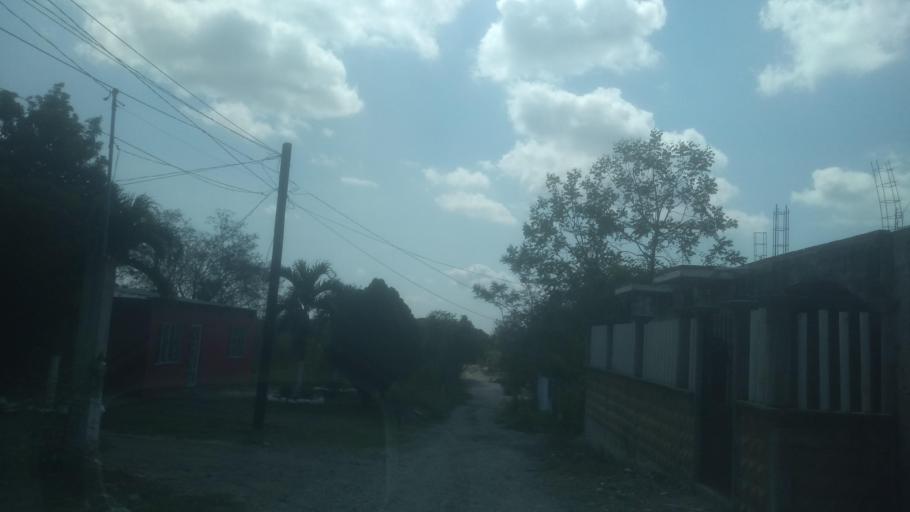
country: MX
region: Veracruz
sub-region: Emiliano Zapata
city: Plan del Rio
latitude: 19.3931
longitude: -96.6345
